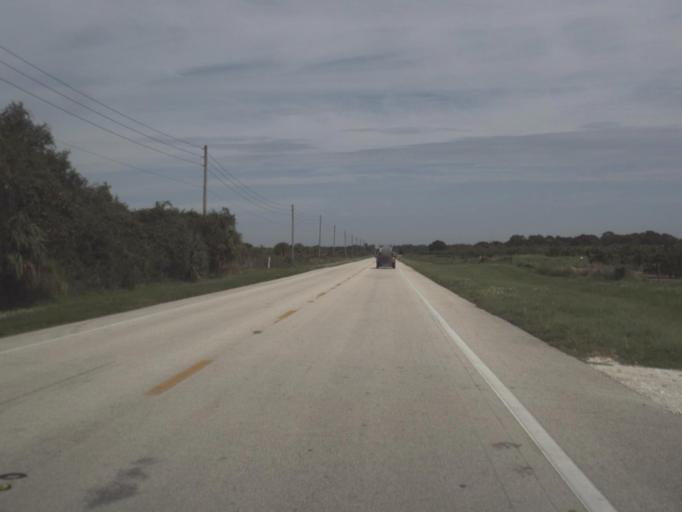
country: US
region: Florida
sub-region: DeSoto County
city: Nocatee
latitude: 27.0557
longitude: -81.7865
